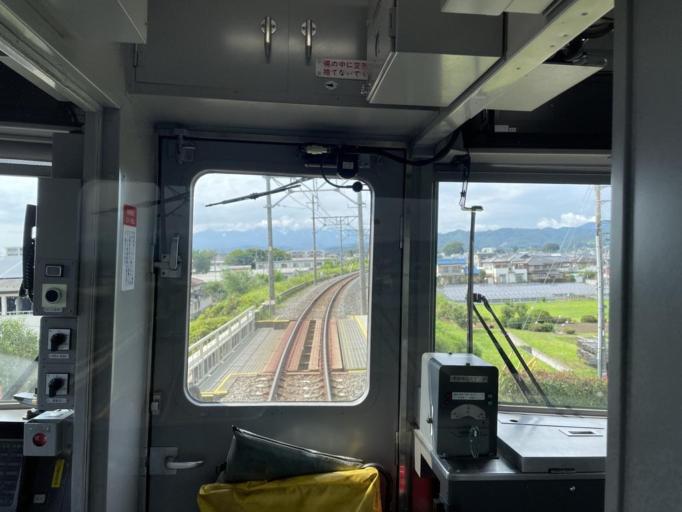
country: JP
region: Gunma
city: Kiryu
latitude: 36.4018
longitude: 139.3134
